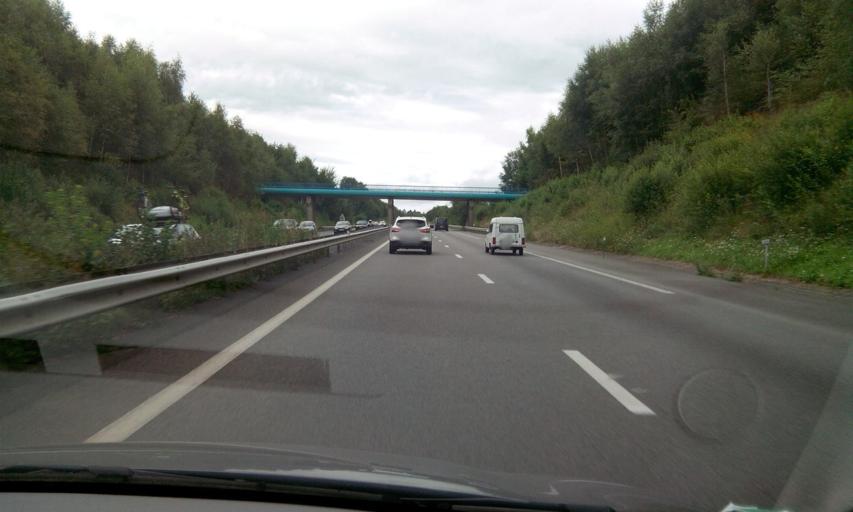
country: FR
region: Limousin
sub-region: Departement de la Correze
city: Uzerche
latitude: 45.4418
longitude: 1.5106
